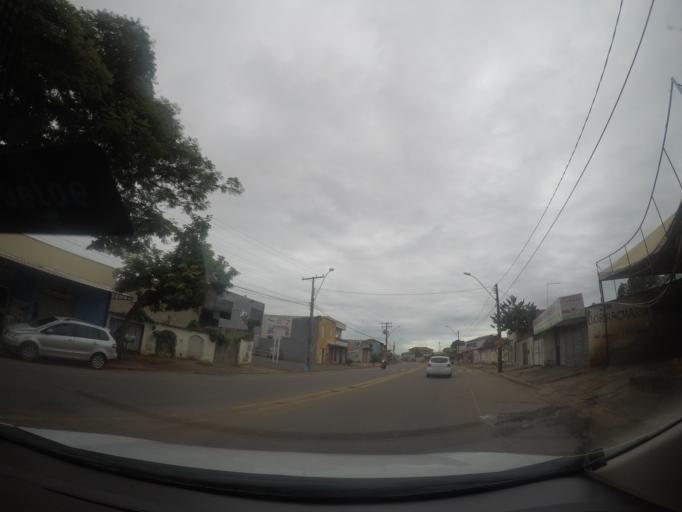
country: BR
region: Goias
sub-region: Goiania
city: Goiania
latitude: -16.6158
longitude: -49.2946
